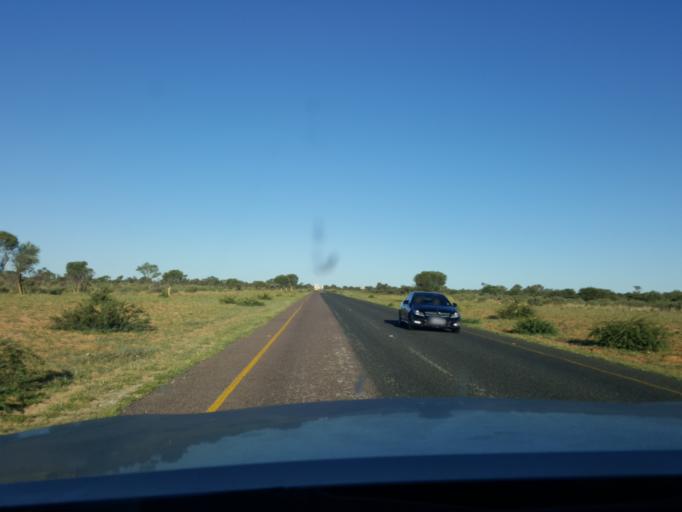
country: BW
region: Southern
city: Khakhea
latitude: -24.2592
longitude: 23.3111
